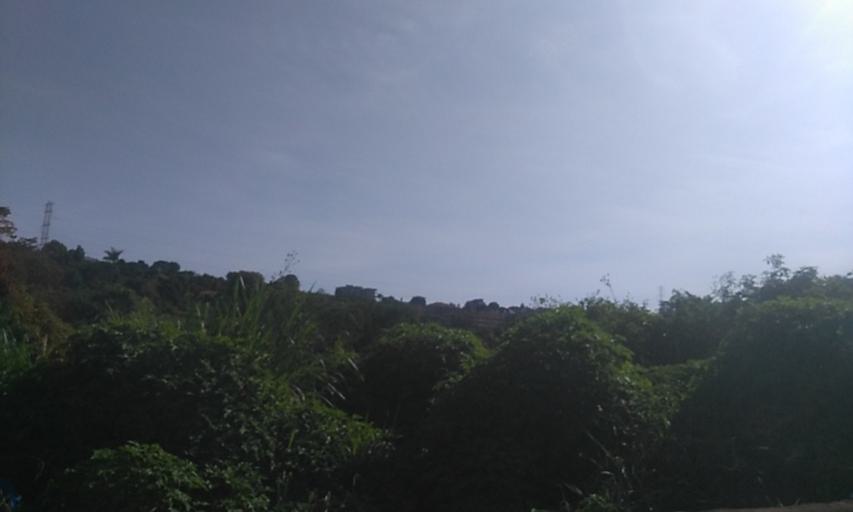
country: UG
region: Central Region
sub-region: Wakiso District
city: Kireka
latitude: 0.3636
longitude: 32.6312
